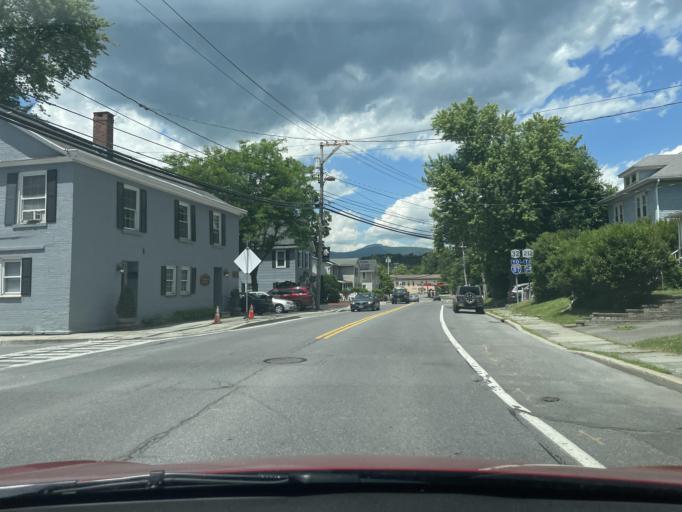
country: US
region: New York
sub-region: Ulster County
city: Saugerties
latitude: 42.0795
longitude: -73.9582
